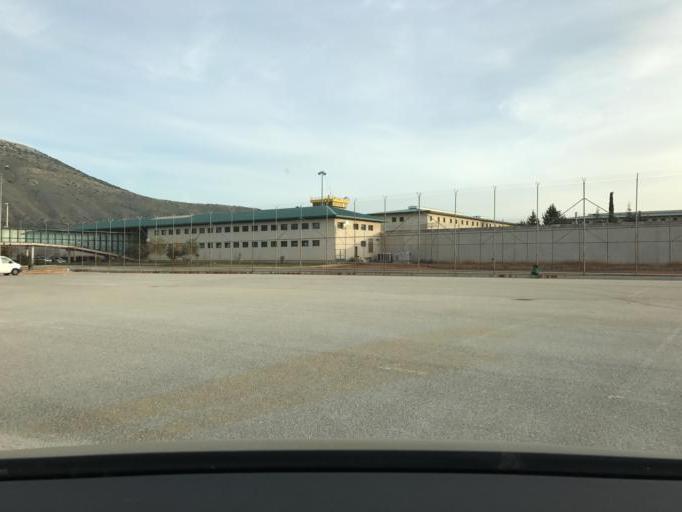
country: ES
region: Andalusia
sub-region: Provincia de Granada
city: Colomera
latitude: 37.3282
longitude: -3.6755
